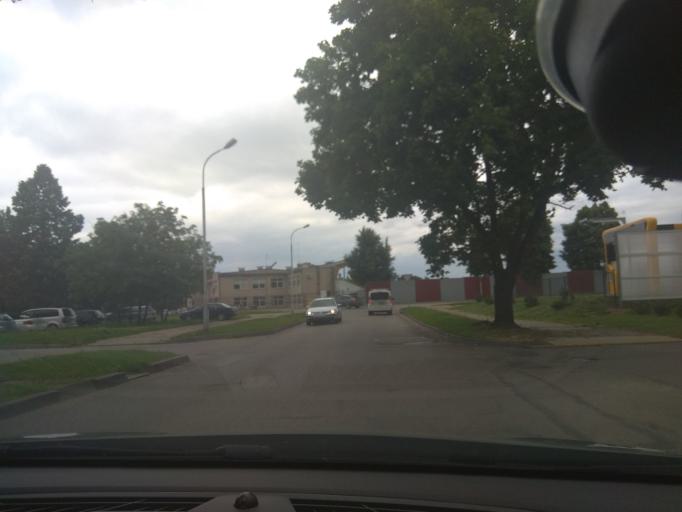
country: LT
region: Marijampoles apskritis
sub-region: Marijampole Municipality
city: Marijampole
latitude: 54.5673
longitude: 23.3625
